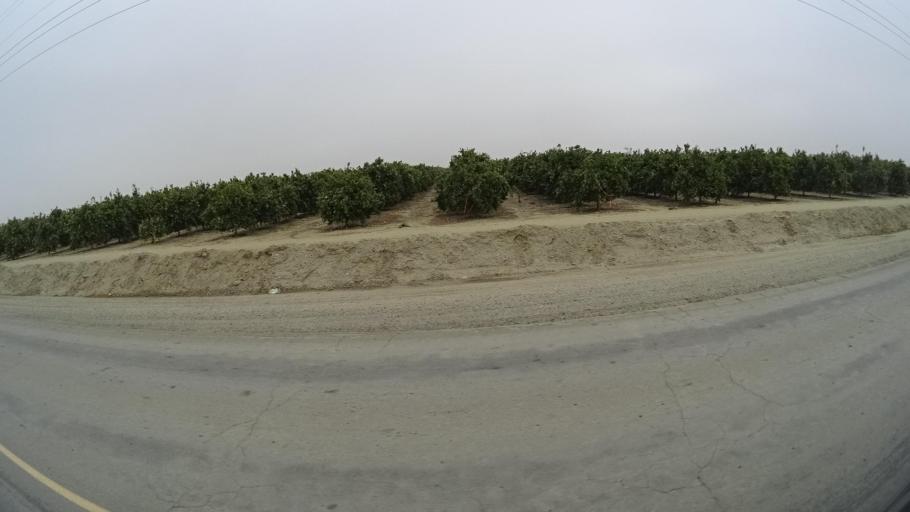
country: US
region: California
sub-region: Kern County
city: Greenfield
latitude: 35.0946
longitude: -119.1025
